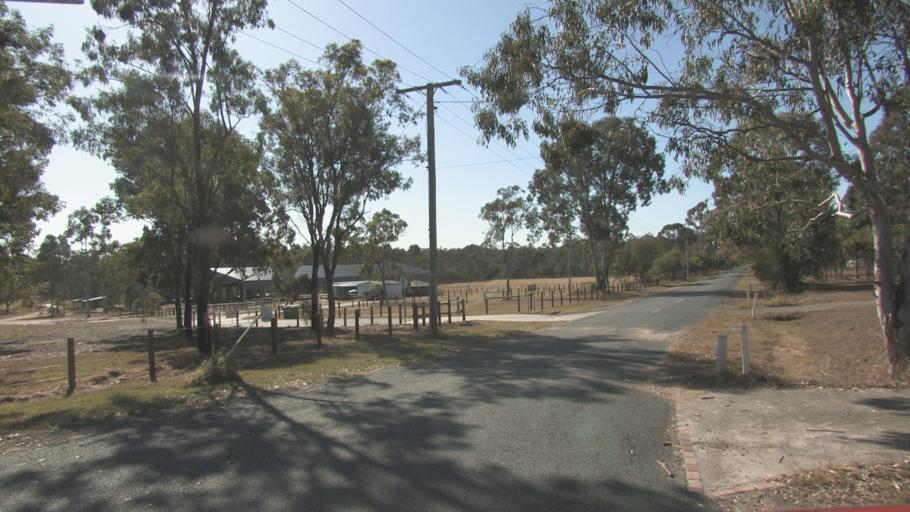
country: AU
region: Queensland
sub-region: Logan
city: Cedar Vale
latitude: -27.8411
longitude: 153.0268
